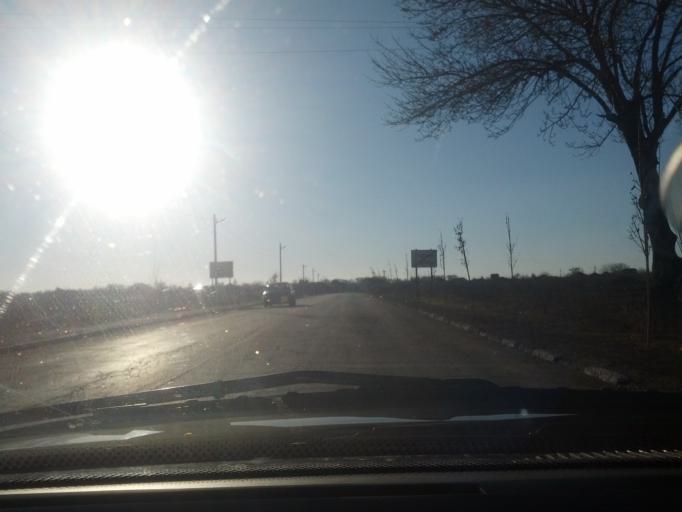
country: BG
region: Vratsa
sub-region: Obshtina Miziya
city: Miziya
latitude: 43.7024
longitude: 23.8228
